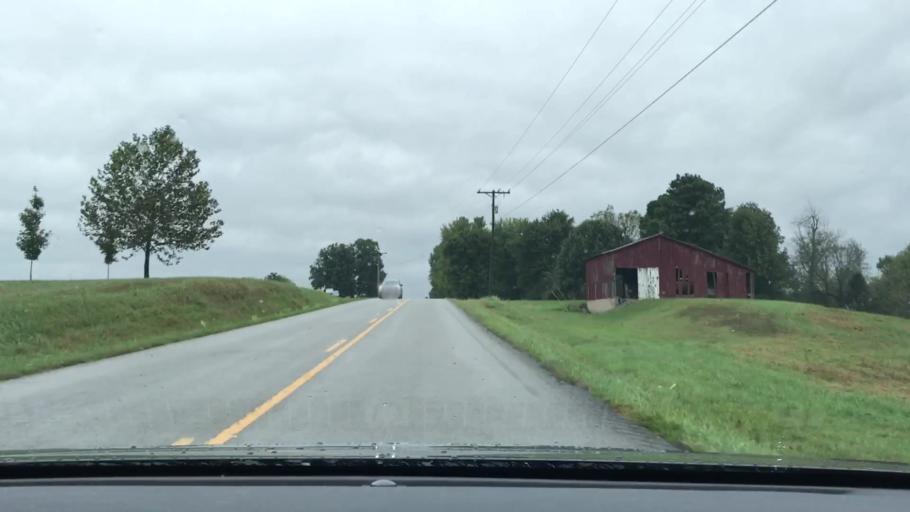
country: US
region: Kentucky
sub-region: McLean County
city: Calhoun
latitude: 37.4626
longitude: -87.2332
